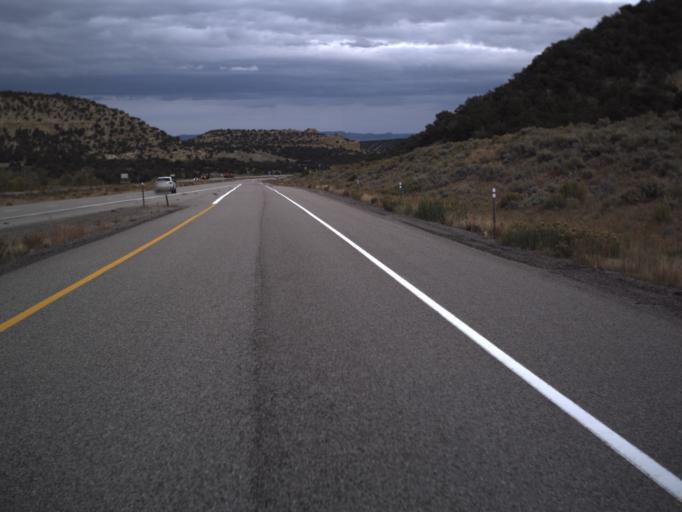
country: US
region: Utah
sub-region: Wayne County
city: Loa
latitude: 38.7569
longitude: -111.4190
